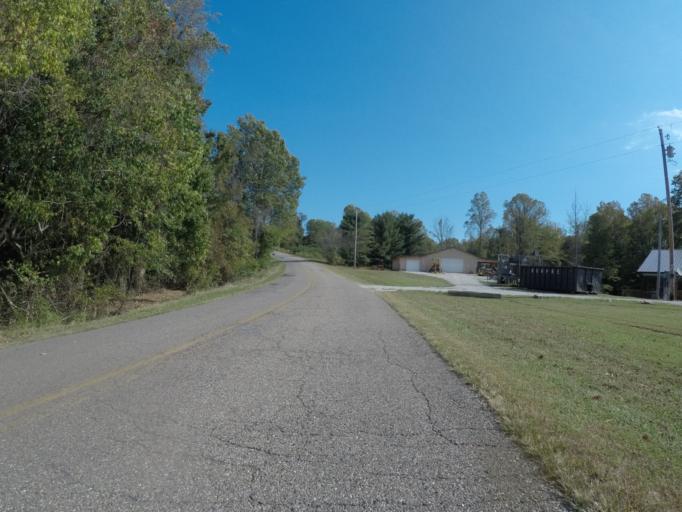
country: US
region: West Virginia
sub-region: Cabell County
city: Lesage
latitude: 38.5973
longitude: -82.4148
